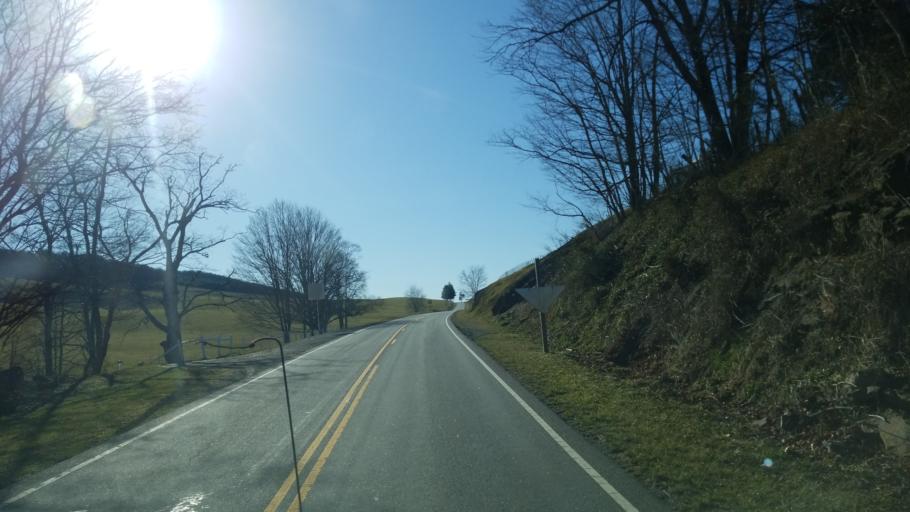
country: US
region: Virginia
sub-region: Giles County
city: Narrows
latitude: 37.1847
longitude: -80.8566
